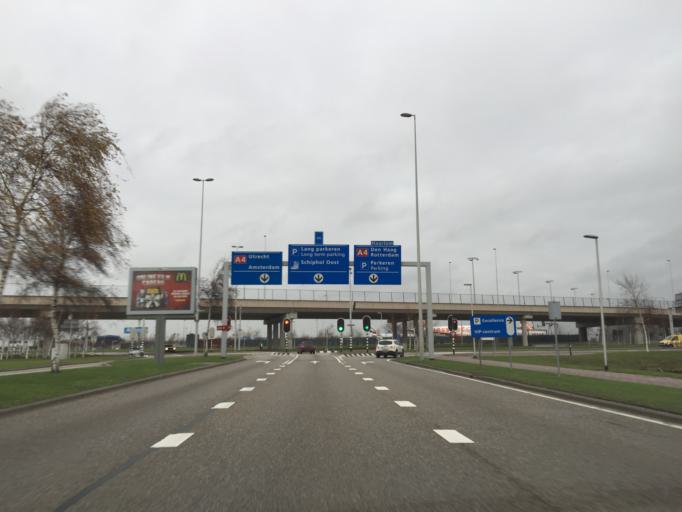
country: NL
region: North Holland
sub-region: Gemeente Aalsmeer
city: Aalsmeer
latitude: 52.3073
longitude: 4.7500
